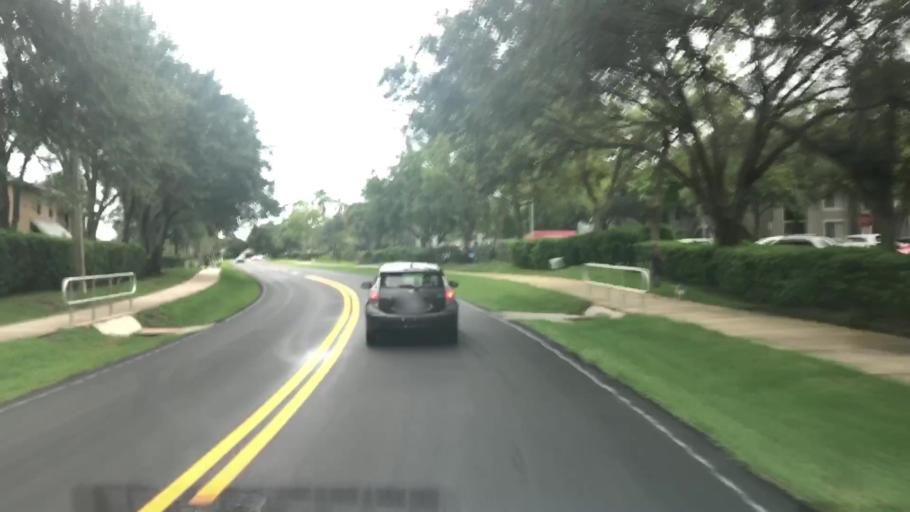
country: US
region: Florida
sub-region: Palm Beach County
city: Boca Pointe
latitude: 26.2990
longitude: -80.1846
